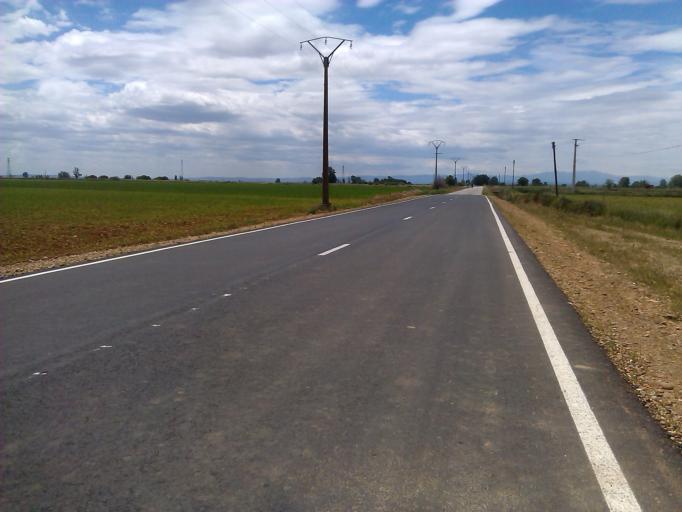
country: ES
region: Castille and Leon
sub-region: Provincia de Leon
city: Bustillo del Paramo
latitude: 42.4638
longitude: -5.7897
